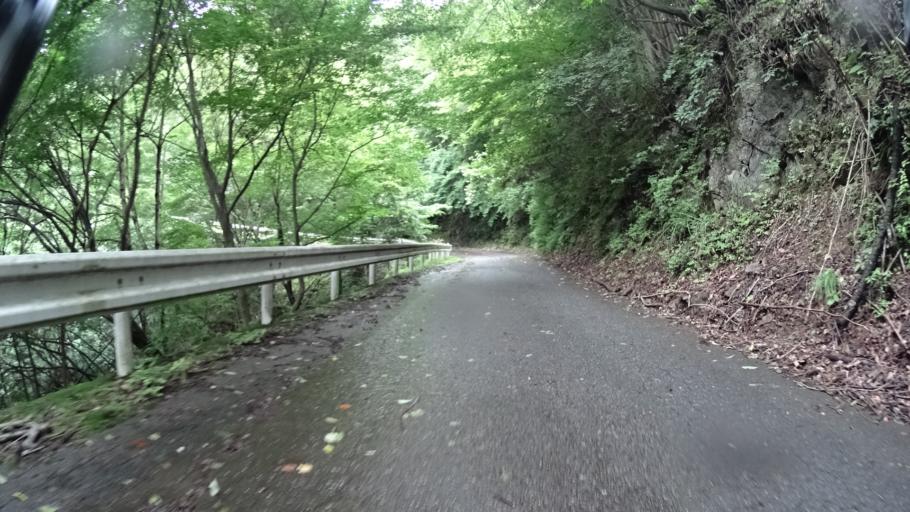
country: JP
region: Saitama
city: Chichibu
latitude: 35.8949
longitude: 139.1282
